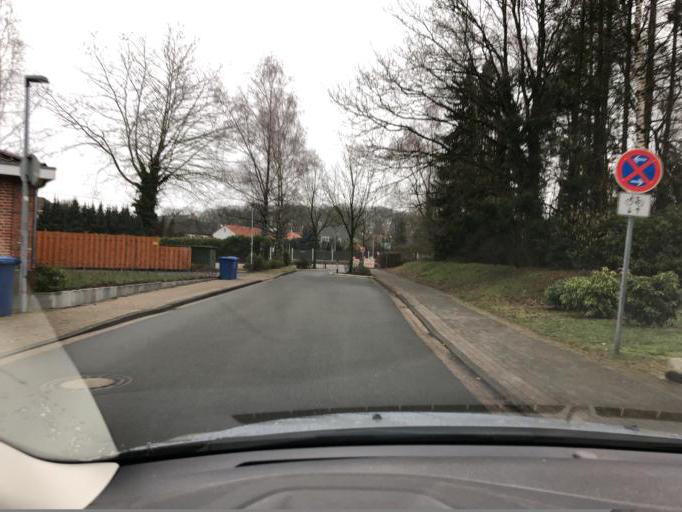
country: DE
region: Lower Saxony
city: Bad Zwischenahn
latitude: 53.1800
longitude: 8.0142
